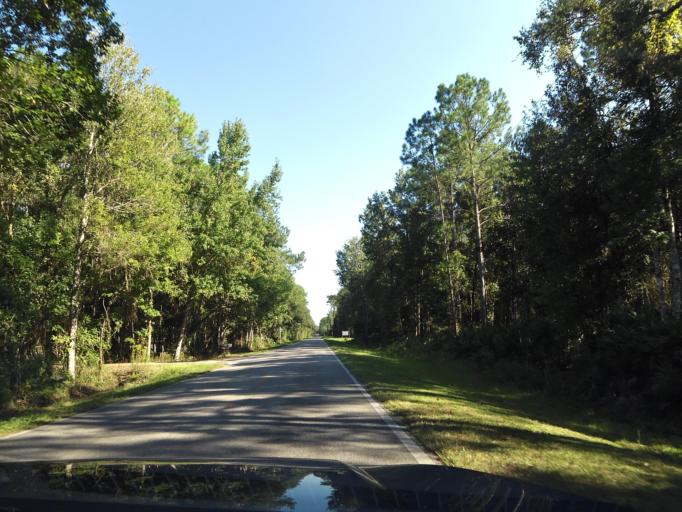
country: US
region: Florida
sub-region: Putnam County
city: East Palatka
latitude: 29.7838
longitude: -81.4927
